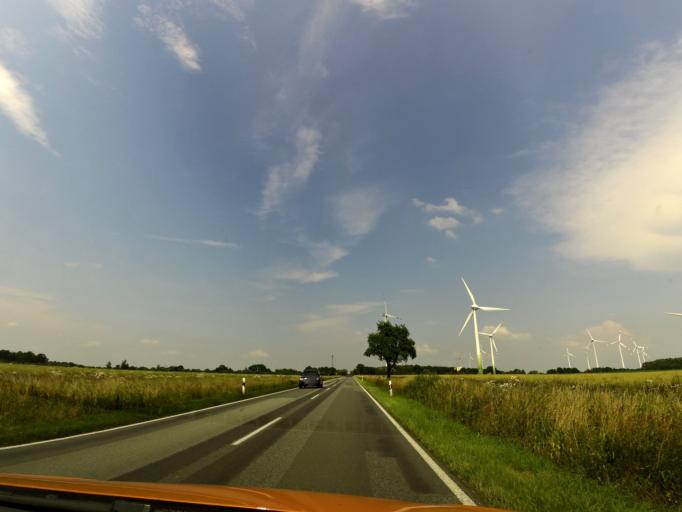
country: DE
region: Brandenburg
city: Gerdshagen
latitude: 53.2223
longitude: 12.2050
